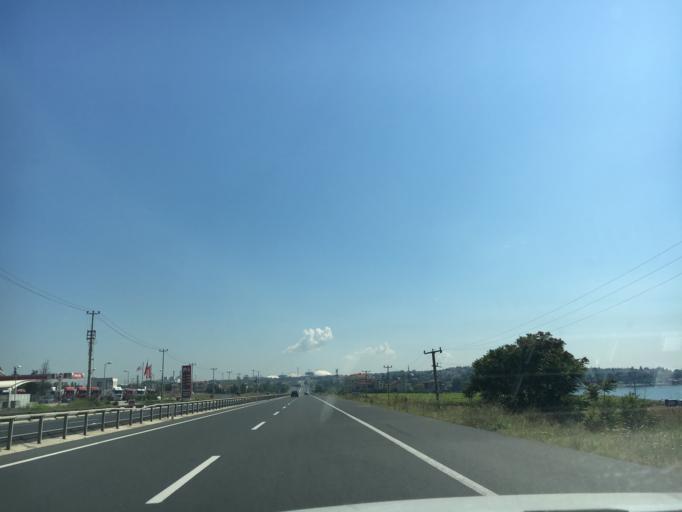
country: TR
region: Tekirdag
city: Marmara Ereglisi
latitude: 40.9816
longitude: 27.9609
